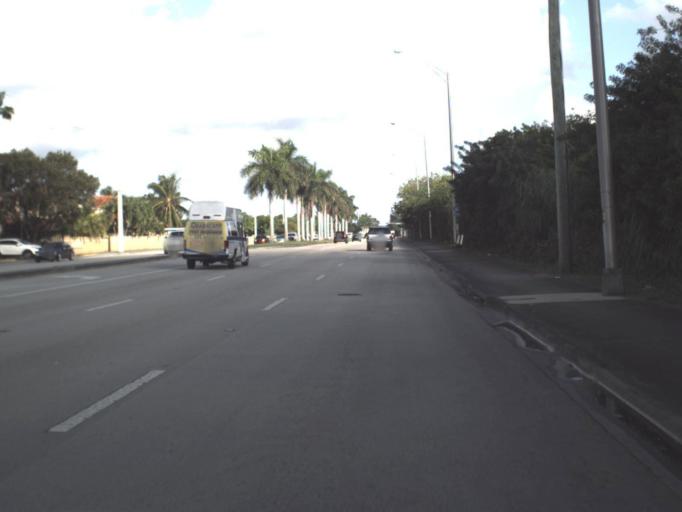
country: US
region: Florida
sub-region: Miami-Dade County
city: Three Lakes
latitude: 25.6265
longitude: -80.4038
